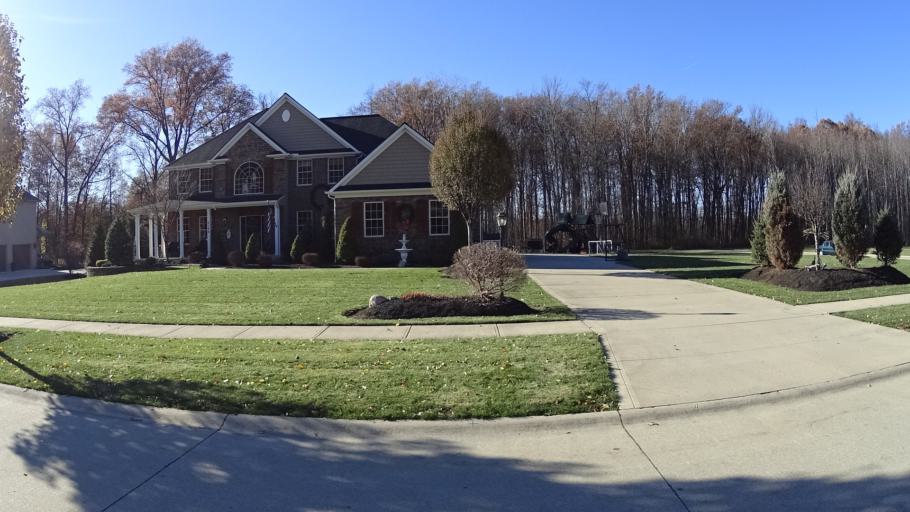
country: US
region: Ohio
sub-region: Lorain County
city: Avon Center
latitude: 41.4450
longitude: -81.9758
